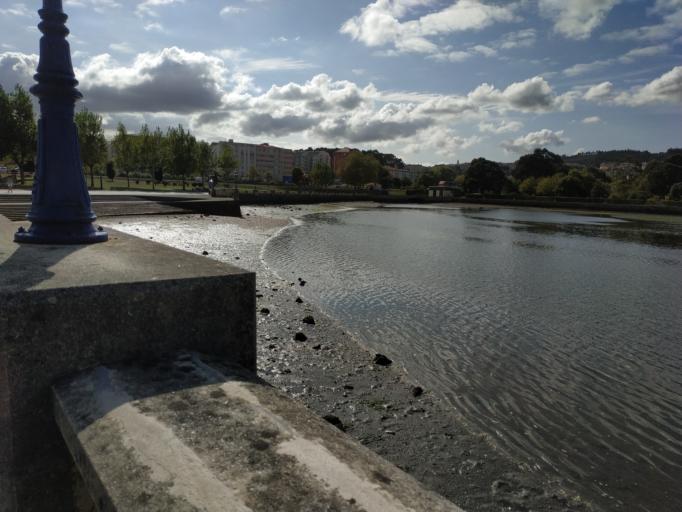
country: ES
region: Galicia
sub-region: Provincia da Coruna
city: Cambre
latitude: 43.3196
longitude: -8.3679
